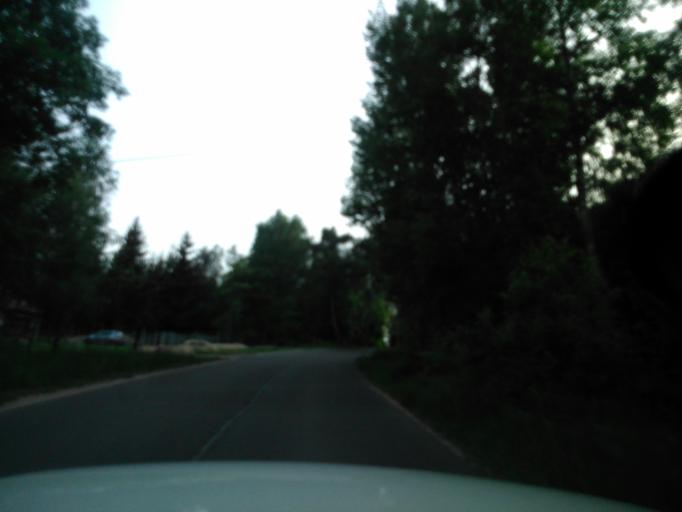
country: PL
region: Kujawsko-Pomorskie
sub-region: Powiat golubsko-dobrzynski
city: Kowalewo Pomorskie
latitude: 53.1401
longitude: 18.9665
